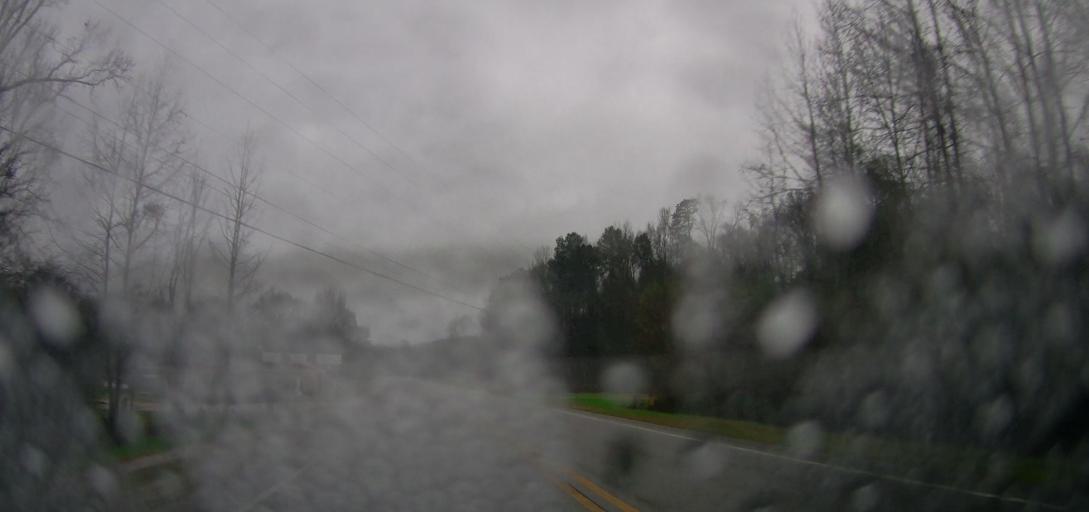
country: US
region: Alabama
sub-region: Autauga County
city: Prattville
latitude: 32.5010
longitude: -86.5842
